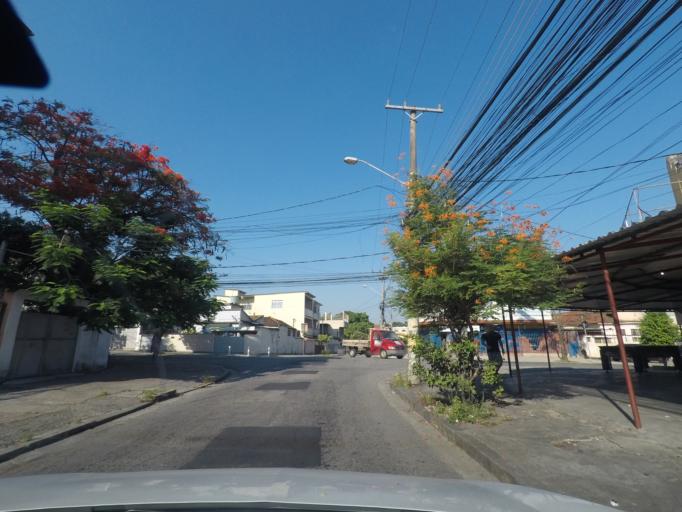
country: BR
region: Rio de Janeiro
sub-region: Duque De Caxias
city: Duque de Caxias
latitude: -22.8282
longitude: -43.2855
